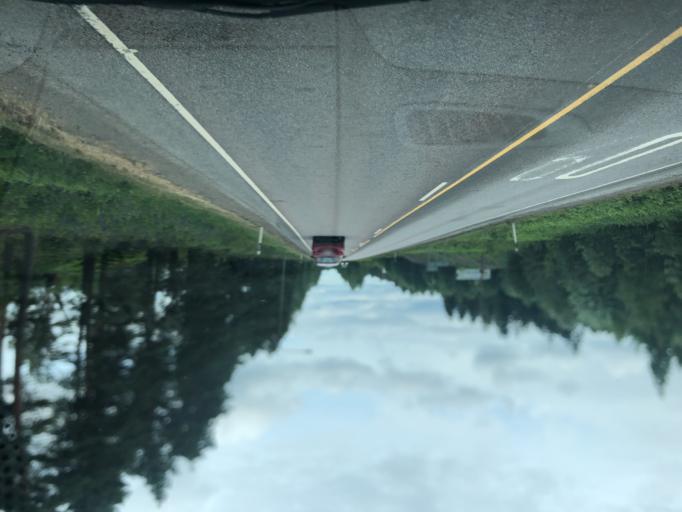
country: FI
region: Kymenlaakso
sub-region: Kouvola
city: Kouvola
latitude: 60.9136
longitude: 26.7709
